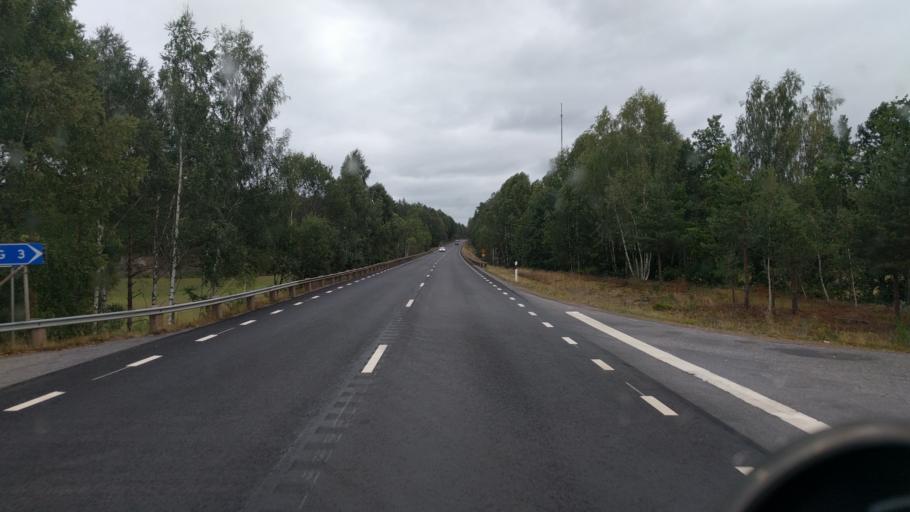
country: SE
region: Kalmar
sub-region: Vasterviks Kommun
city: Ankarsrum
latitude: 57.7244
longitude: 16.4001
